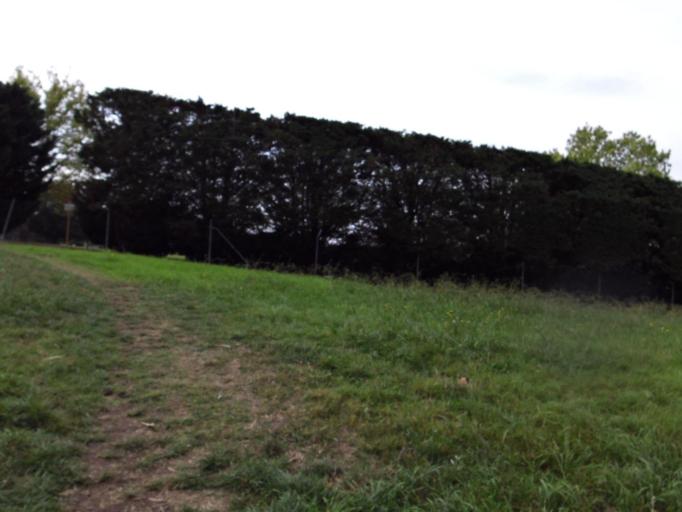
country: AU
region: Victoria
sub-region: Casey
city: Berwick
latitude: -38.0427
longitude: 145.3623
